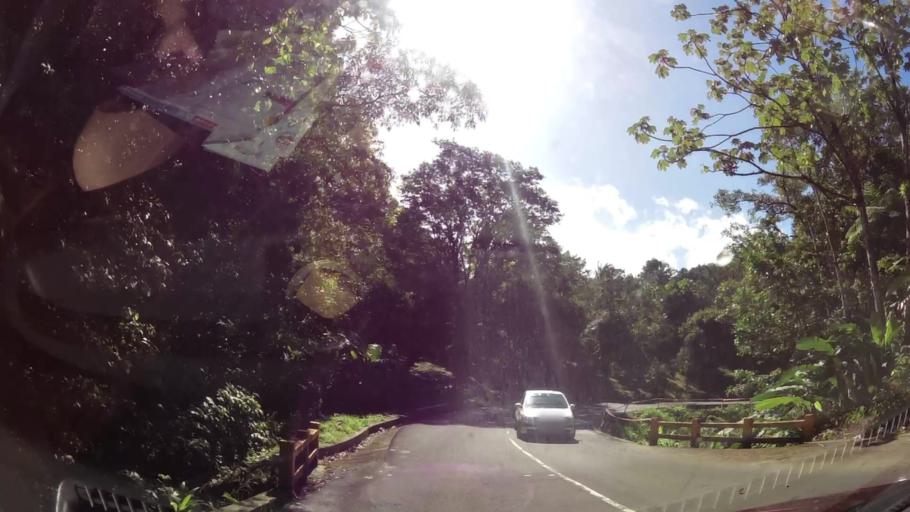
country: DM
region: Saint Paul
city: Pont Casse
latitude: 15.3684
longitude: -61.3522
